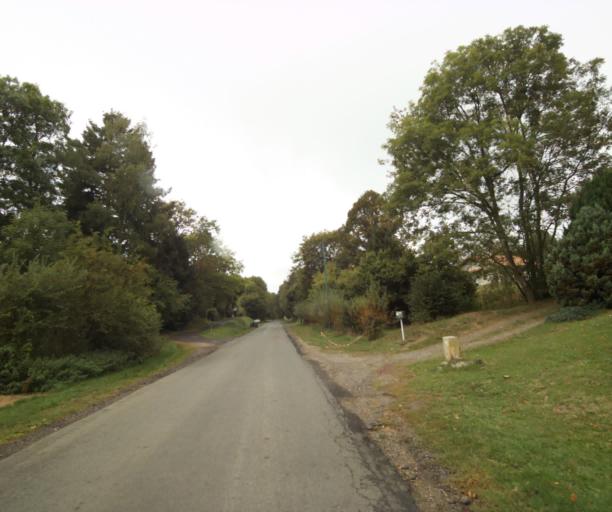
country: FR
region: Auvergne
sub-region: Departement du Puy-de-Dome
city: Saint-Genes-Champanelle
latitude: 45.7279
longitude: 2.9886
